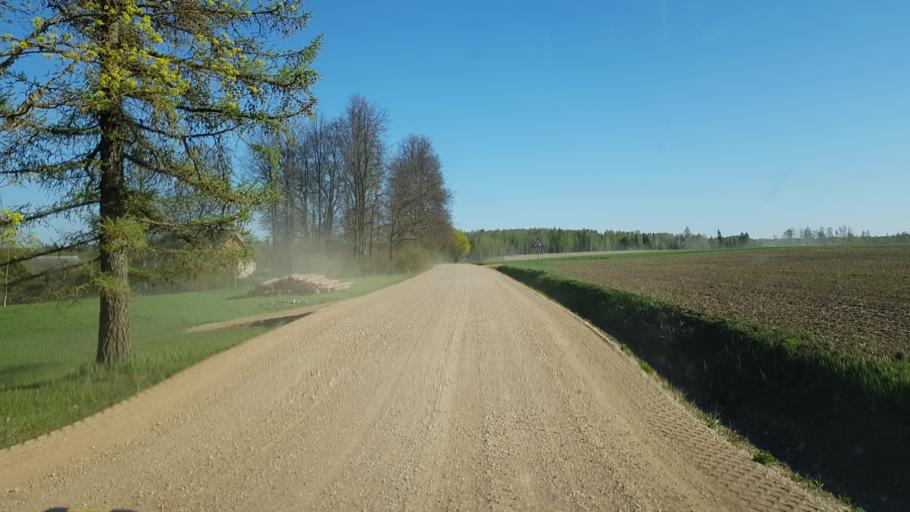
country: EE
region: Polvamaa
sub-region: Polva linn
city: Polva
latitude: 58.1007
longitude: 27.2240
